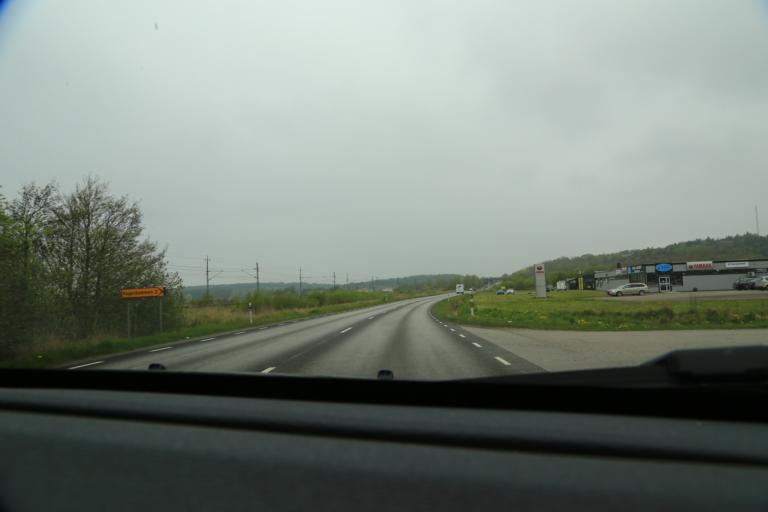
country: SE
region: Halland
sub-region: Varbergs Kommun
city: Varberg
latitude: 57.1654
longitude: 12.2358
